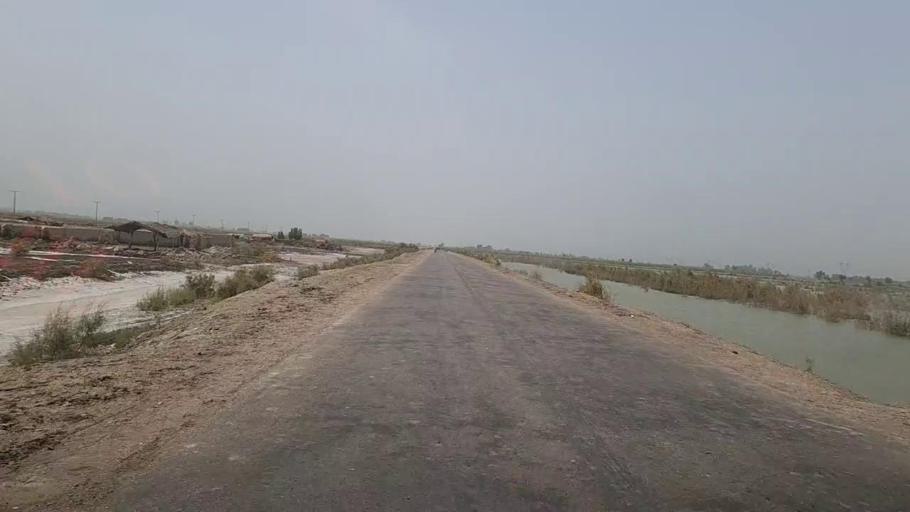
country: PK
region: Sindh
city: Radhan
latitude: 27.1585
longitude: 67.9417
